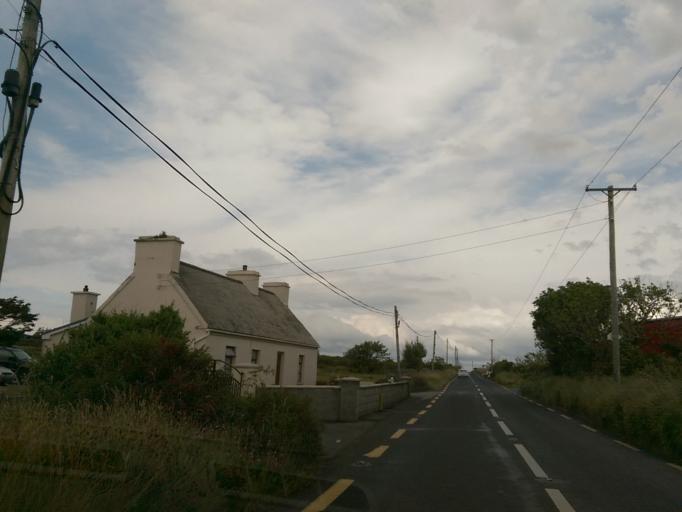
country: IE
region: Munster
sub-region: An Clar
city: Kilrush
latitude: 52.7238
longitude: -9.5710
